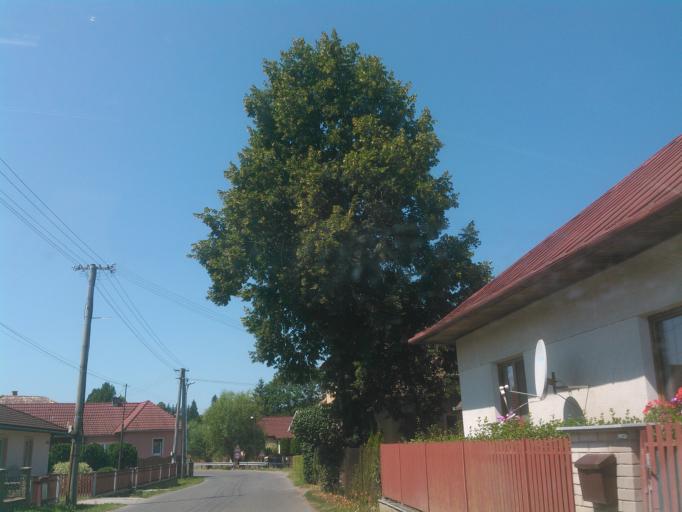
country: SK
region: Zilinsky
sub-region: Okres Liptovsky Mikulas
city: Liptovsky Mikulas
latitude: 49.0530
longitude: 19.4807
